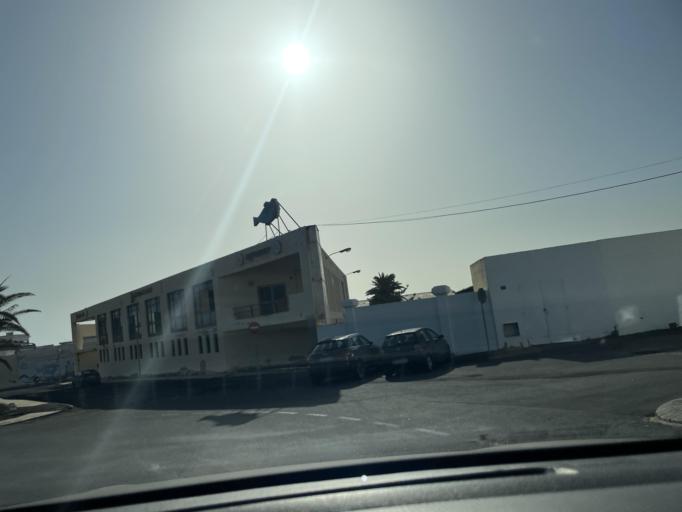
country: ES
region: Canary Islands
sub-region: Provincia de Las Palmas
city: Arrecife
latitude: 28.9691
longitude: -13.5383
